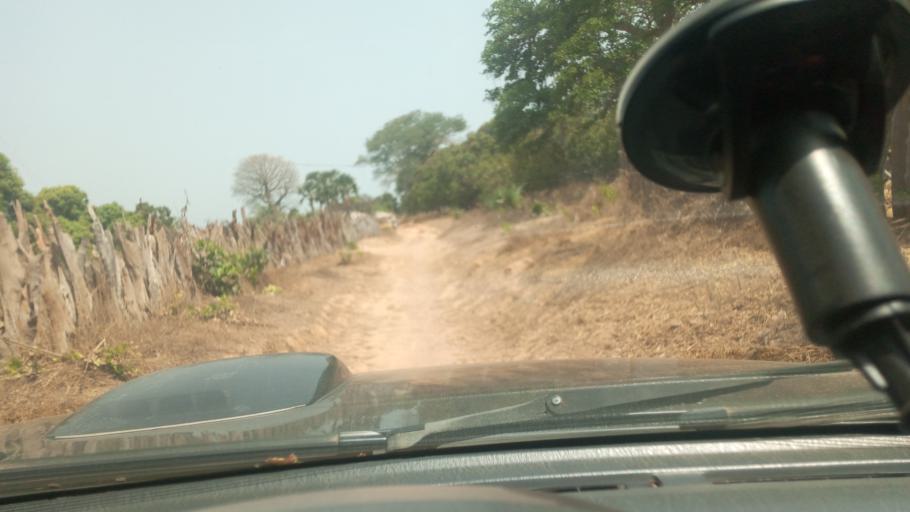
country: GW
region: Oio
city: Bissora
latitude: 12.4398
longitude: -15.6155
